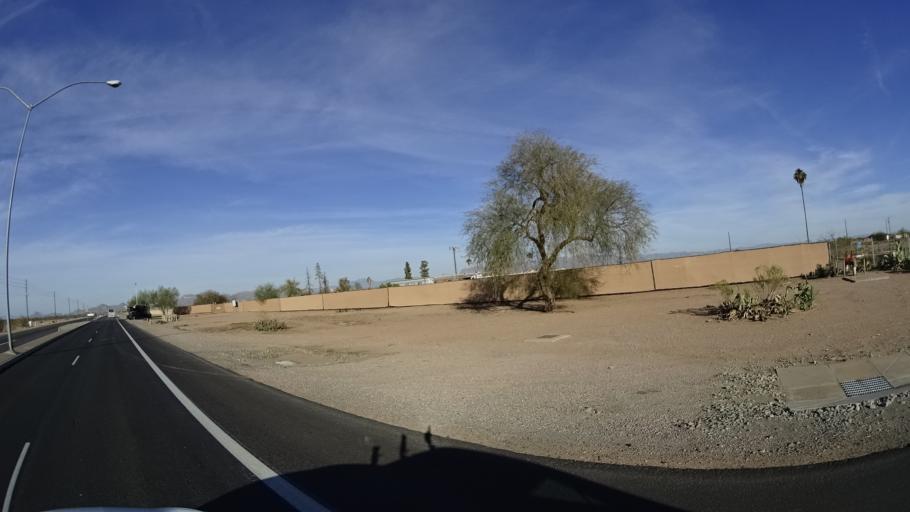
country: US
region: Arizona
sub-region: Maricopa County
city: Queen Creek
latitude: 33.3282
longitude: -111.6355
